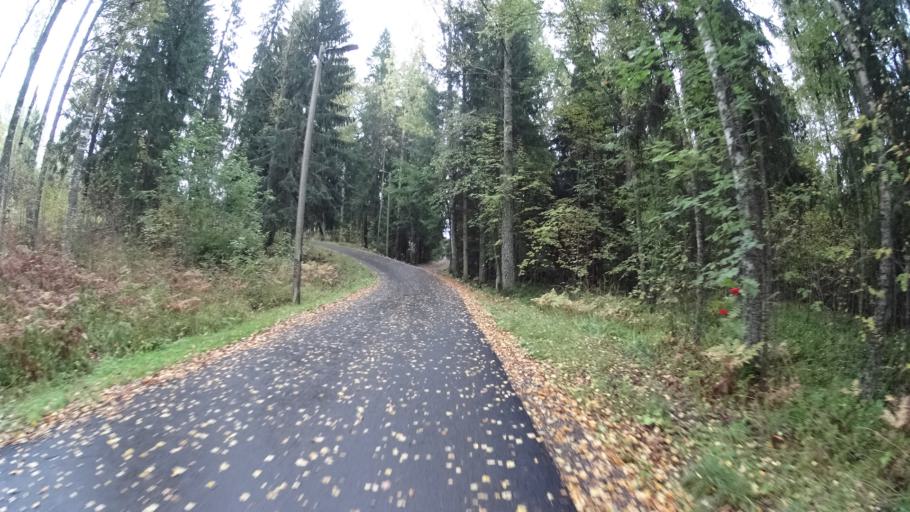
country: FI
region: Uusimaa
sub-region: Helsinki
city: Kauniainen
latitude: 60.3090
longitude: 24.7318
